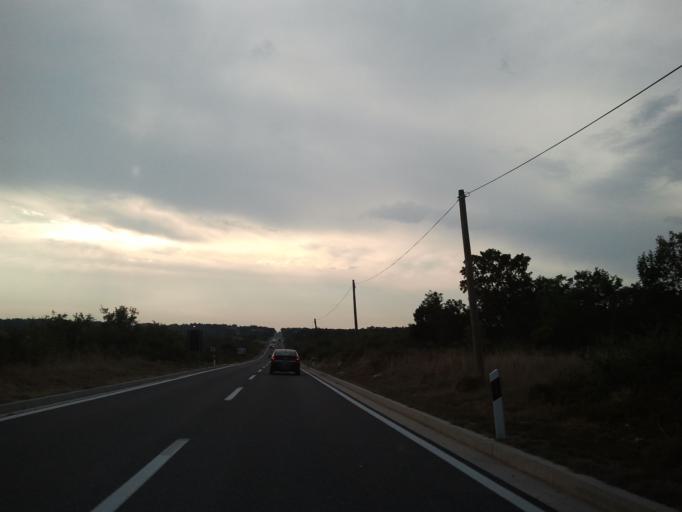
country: HR
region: Zadarska
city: Posedarje
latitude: 44.2282
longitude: 15.4277
